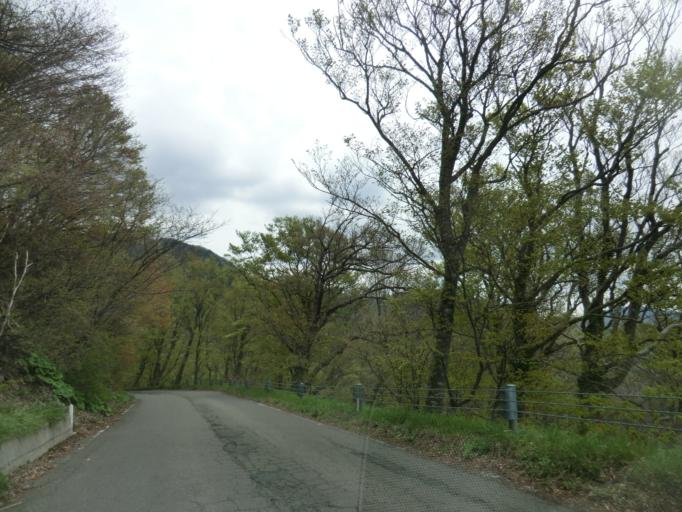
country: JP
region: Aomori
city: Mutsu
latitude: 41.3193
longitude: 140.8049
